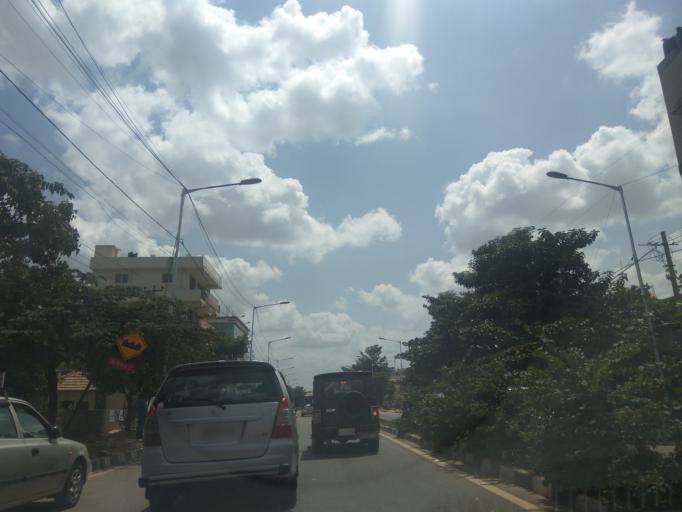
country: IN
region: Karnataka
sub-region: Bangalore Urban
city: Yelahanka
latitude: 13.1218
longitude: 77.6266
